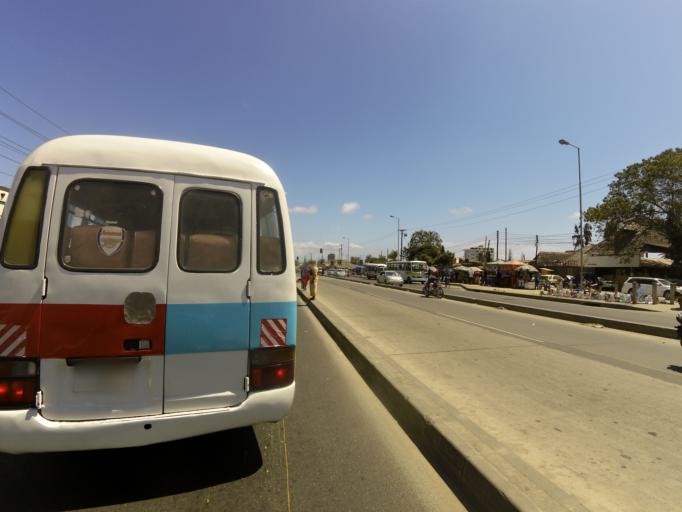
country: TZ
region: Dar es Salaam
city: Magomeni
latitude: -6.7931
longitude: 39.2643
